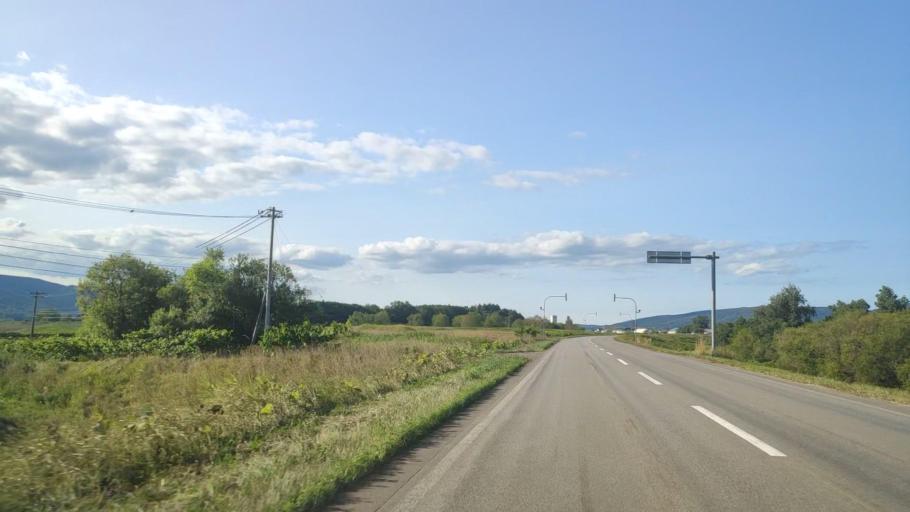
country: JP
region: Hokkaido
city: Nayoro
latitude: 44.8100
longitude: 142.0662
